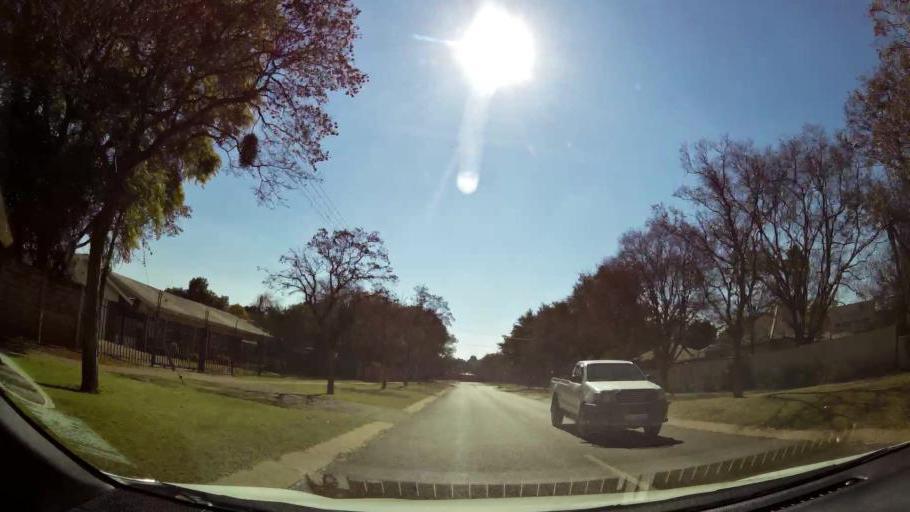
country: ZA
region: Gauteng
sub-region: City of Tshwane Metropolitan Municipality
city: Pretoria
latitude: -25.7479
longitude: 28.2424
